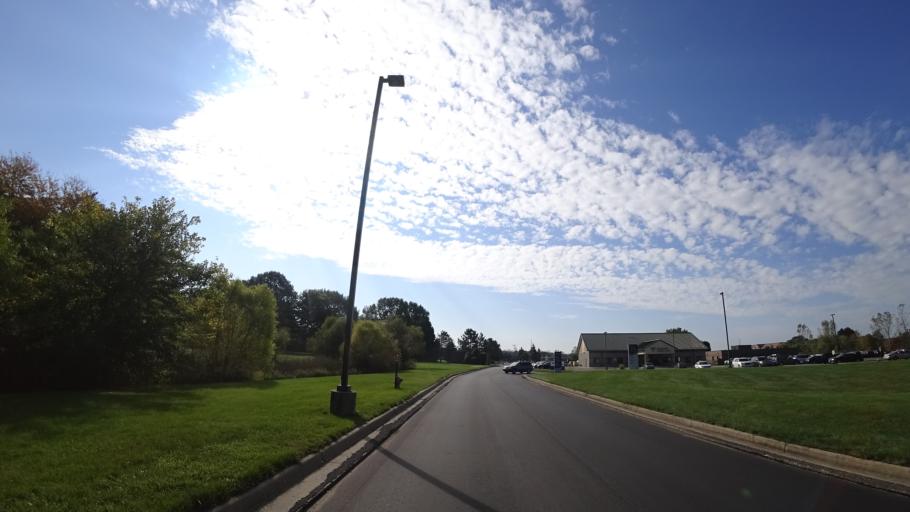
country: US
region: Michigan
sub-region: Saint Joseph County
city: Three Rivers
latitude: 41.9375
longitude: -85.6471
